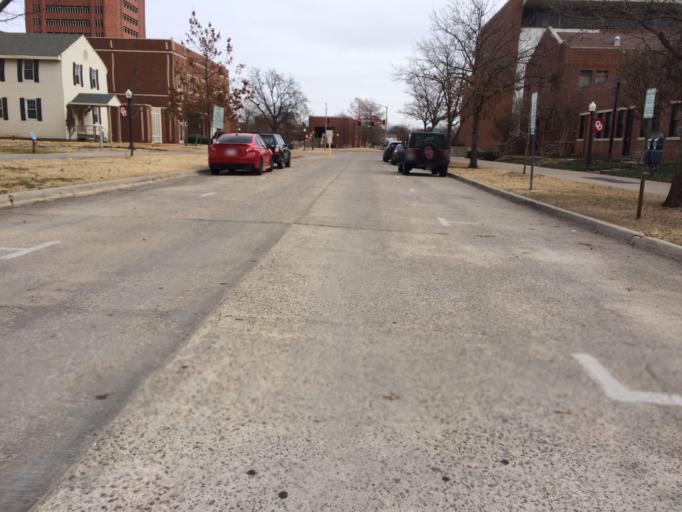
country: US
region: Oklahoma
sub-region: Cleveland County
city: Norman
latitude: 35.2098
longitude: -97.4426
